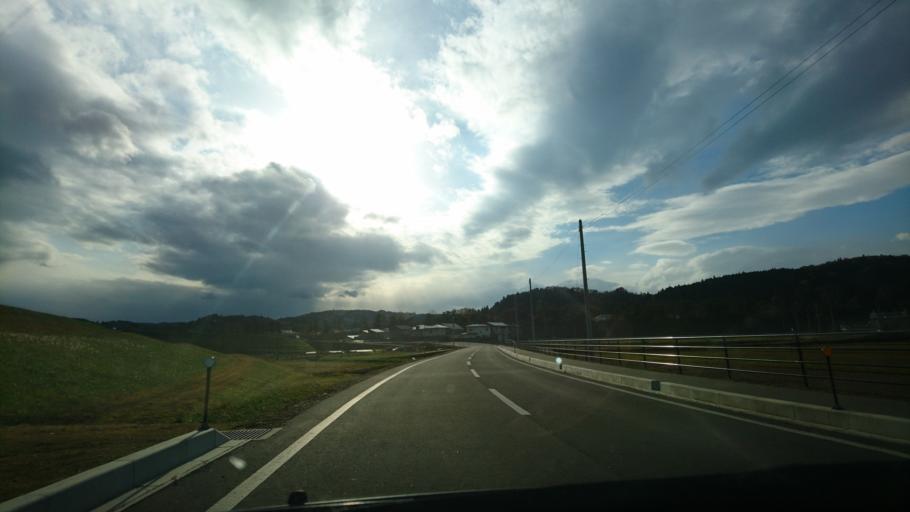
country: JP
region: Iwate
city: Ichinoseki
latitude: 38.9831
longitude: 141.1114
